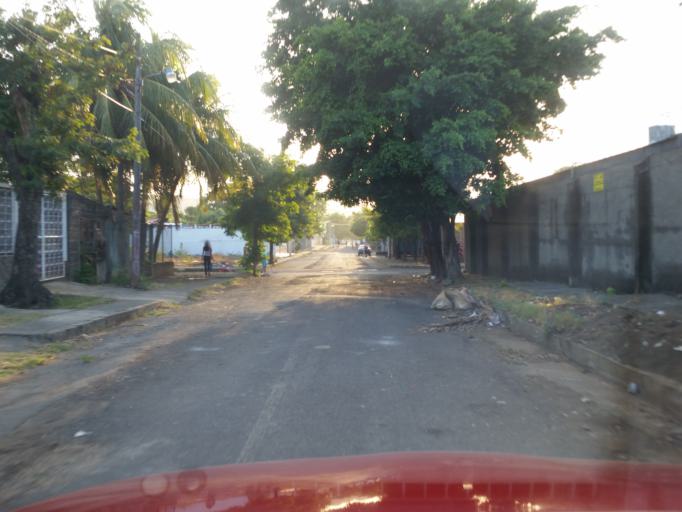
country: NI
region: Managua
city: Managua
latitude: 12.1395
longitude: -86.2620
